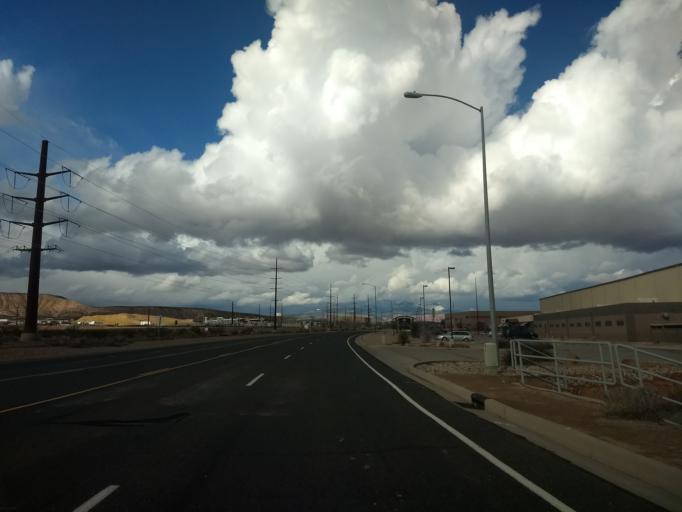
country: US
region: Utah
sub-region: Washington County
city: Saint George
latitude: 37.0270
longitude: -113.5632
